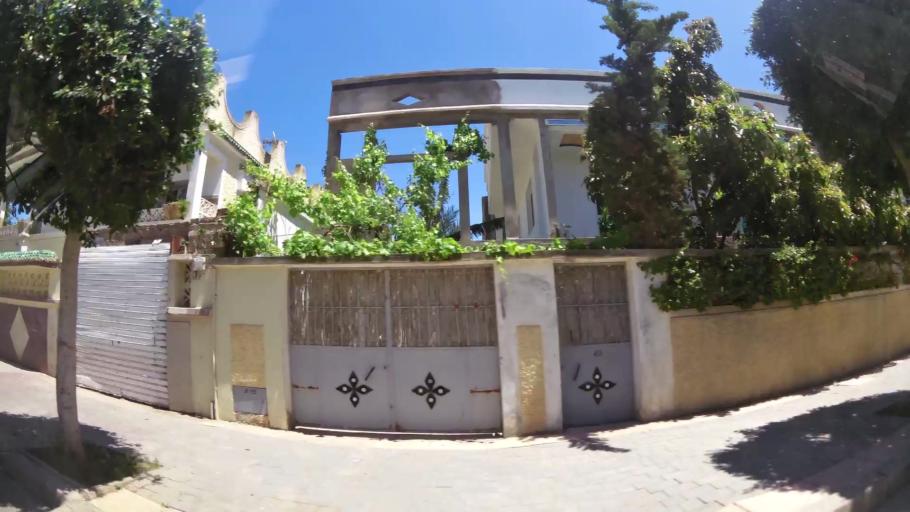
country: MA
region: Oriental
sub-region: Berkane-Taourirt
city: Madagh
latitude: 35.0826
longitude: -2.2217
